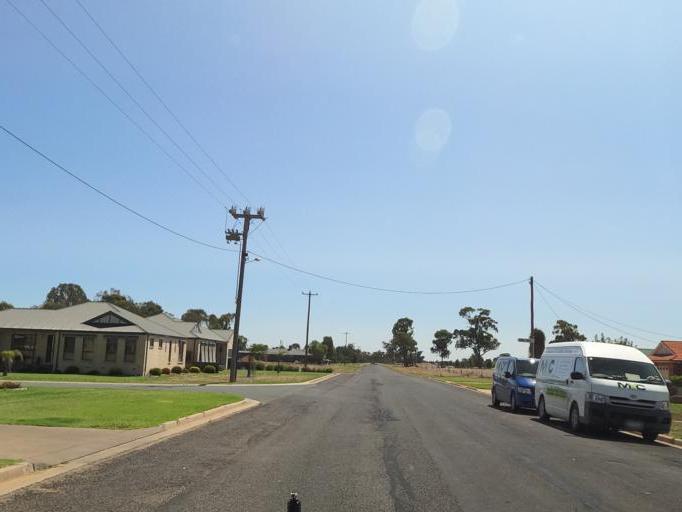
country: AU
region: New South Wales
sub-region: Corowa Shire
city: Mulwala
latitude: -35.9845
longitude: 145.9996
